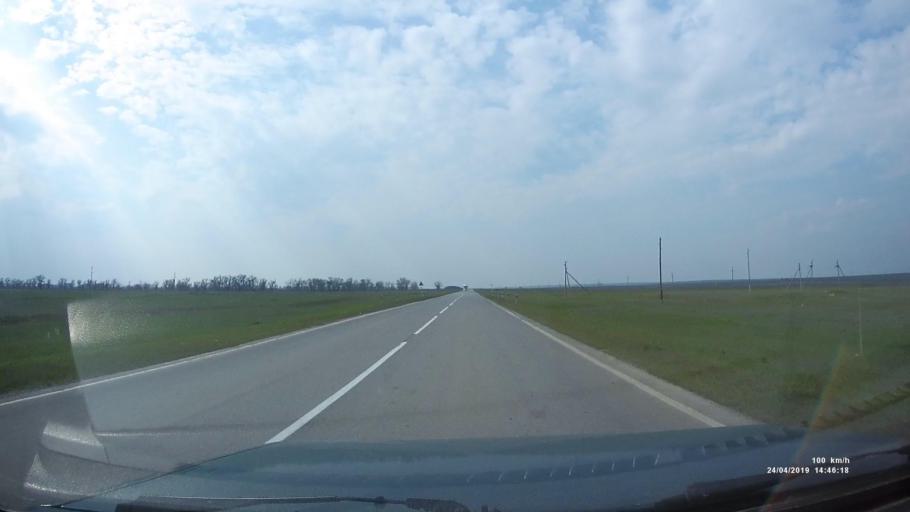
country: RU
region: Rostov
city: Remontnoye
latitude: 46.4807
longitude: 43.7928
